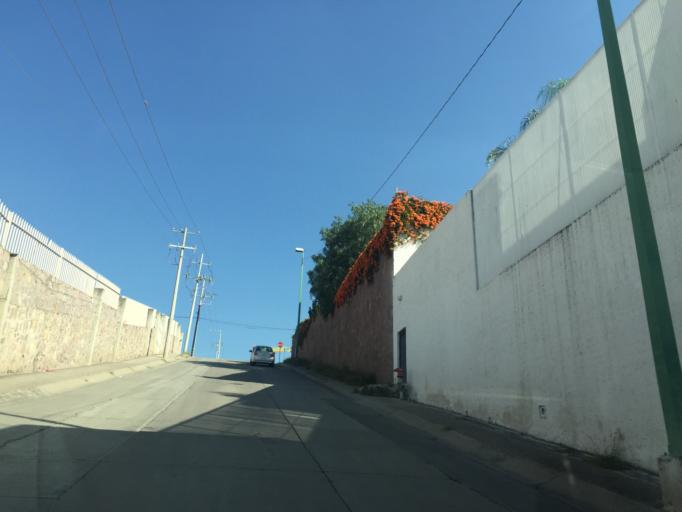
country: MX
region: Guanajuato
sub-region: Leon
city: La Ermita
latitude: 21.1540
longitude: -101.7100
